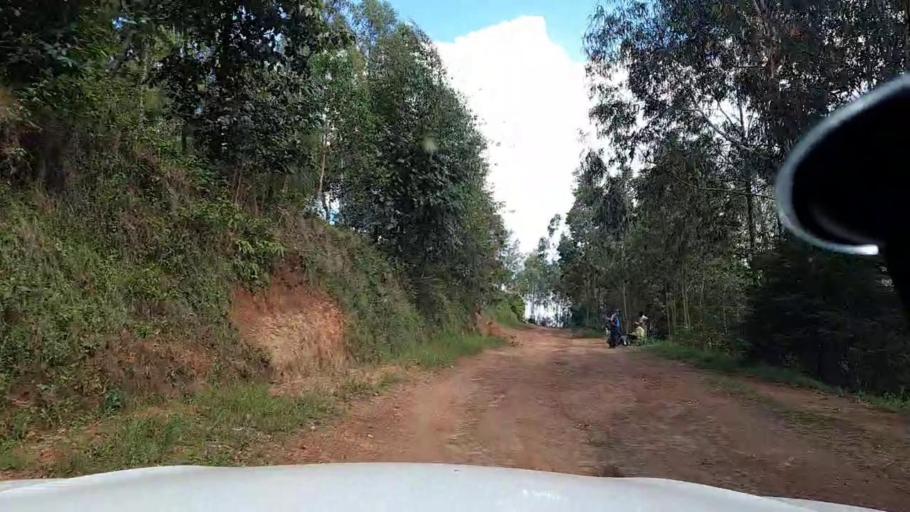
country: RW
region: Kigali
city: Kigali
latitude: -1.7880
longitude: 29.8292
